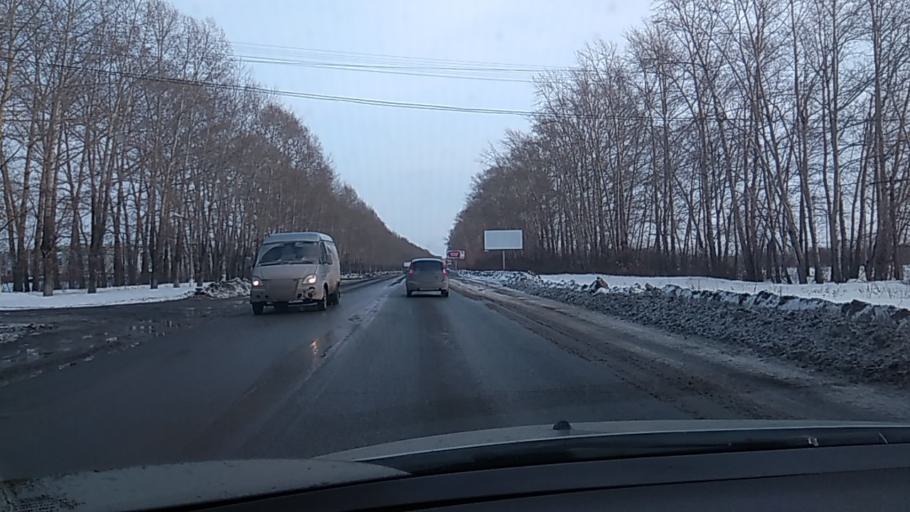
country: RU
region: Sverdlovsk
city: Martyush
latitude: 56.4429
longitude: 61.8266
